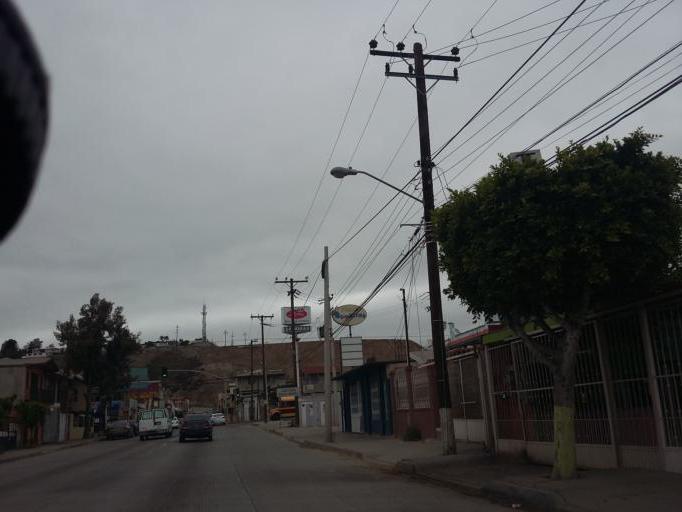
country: MX
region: Baja California
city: Tijuana
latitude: 32.5233
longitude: -116.9254
